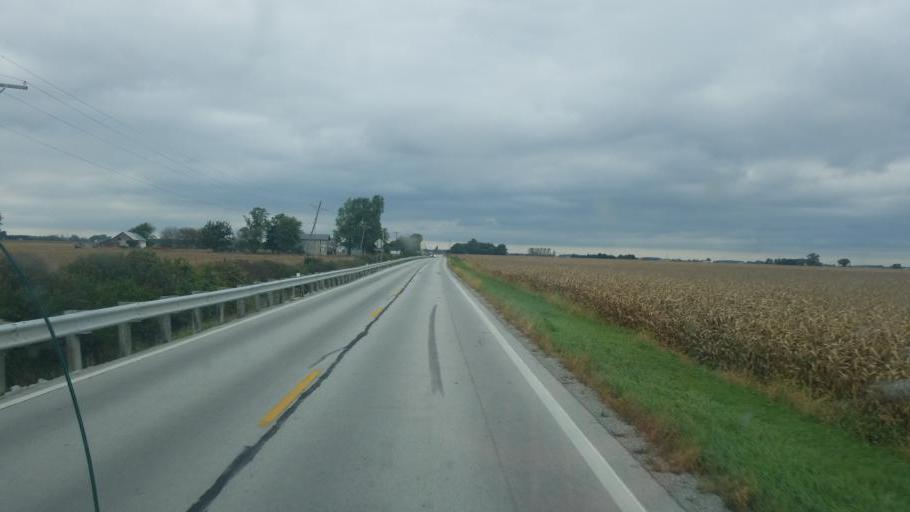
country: US
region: Ohio
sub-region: Wood County
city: Haskins
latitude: 41.4400
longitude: -83.6974
